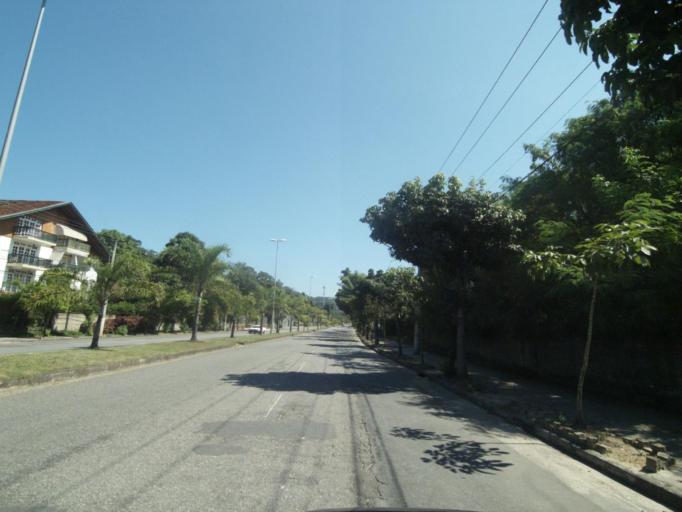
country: BR
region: Rio de Janeiro
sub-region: Sao Goncalo
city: Sao Goncalo
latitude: -22.8908
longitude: -43.0349
